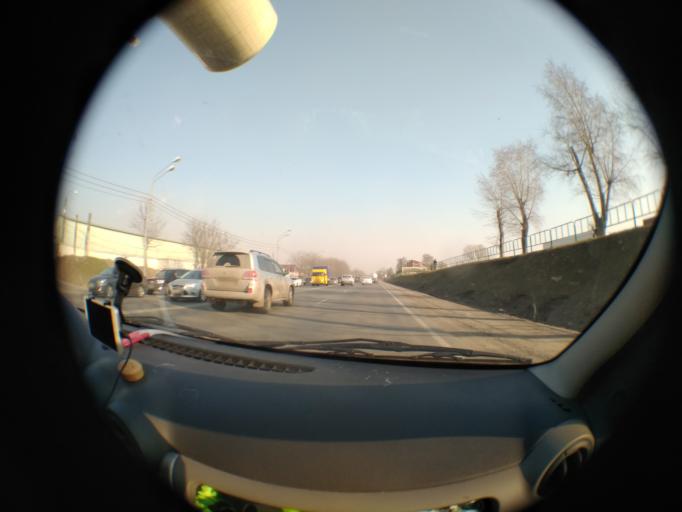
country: RU
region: Moskovskaya
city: Ostrovtsy
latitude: 55.5958
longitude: 37.9912
